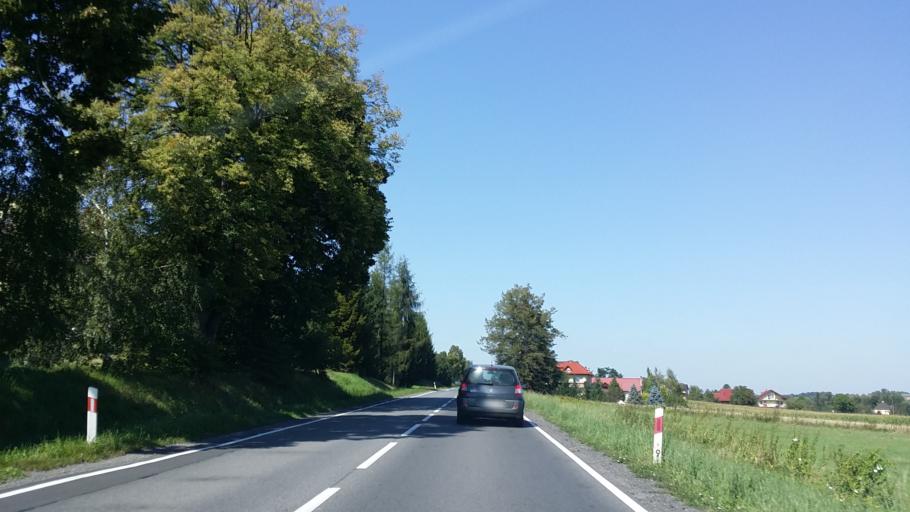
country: PL
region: Lesser Poland Voivodeship
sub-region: Powiat wadowicki
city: Radocza
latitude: 49.9195
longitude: 19.4807
